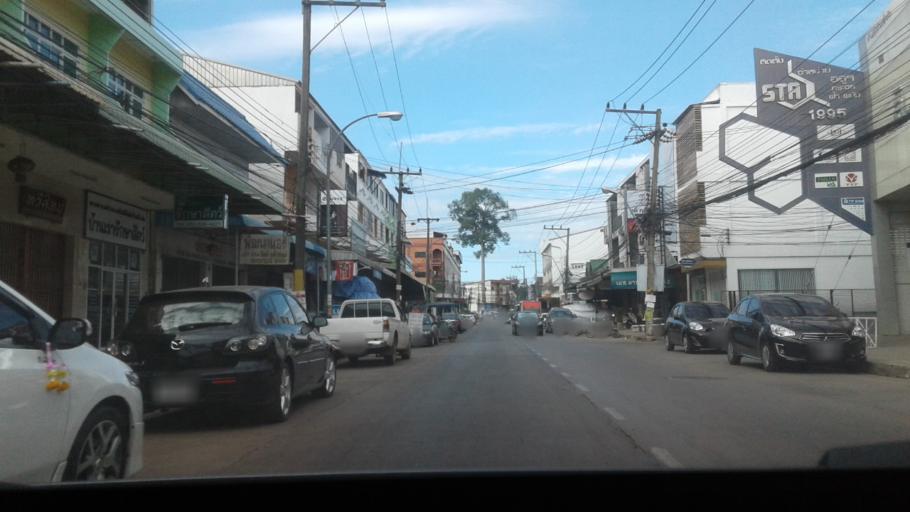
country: TH
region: Changwat Udon Thani
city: Udon Thani
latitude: 17.4153
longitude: 102.8001
